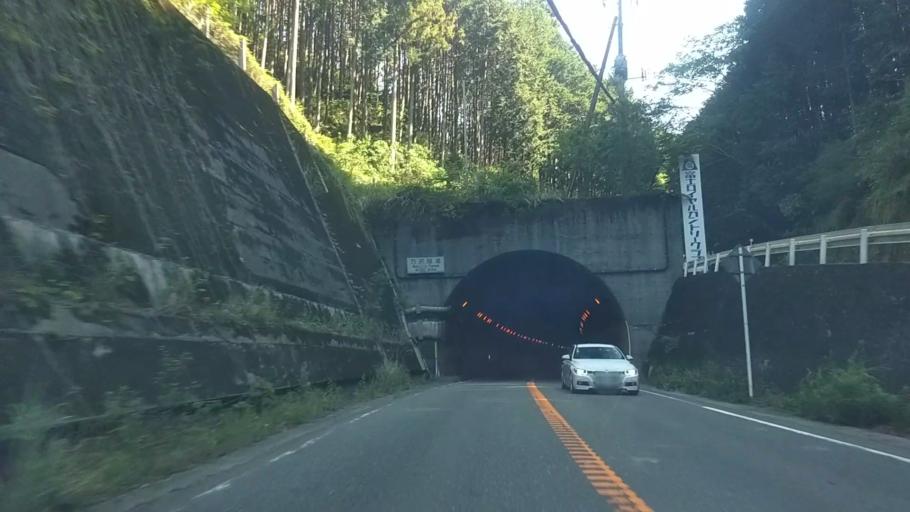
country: JP
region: Shizuoka
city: Fujinomiya
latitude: 35.2061
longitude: 138.5158
